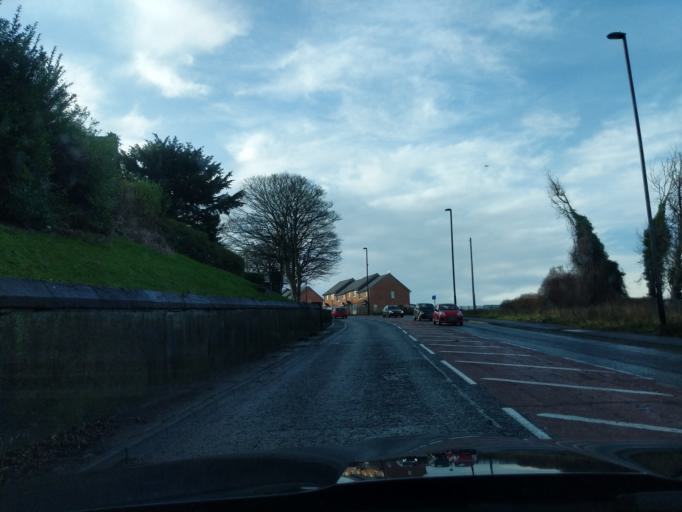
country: GB
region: England
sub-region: Borough of North Tyneside
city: Wallsend
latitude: 54.9954
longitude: -1.5157
